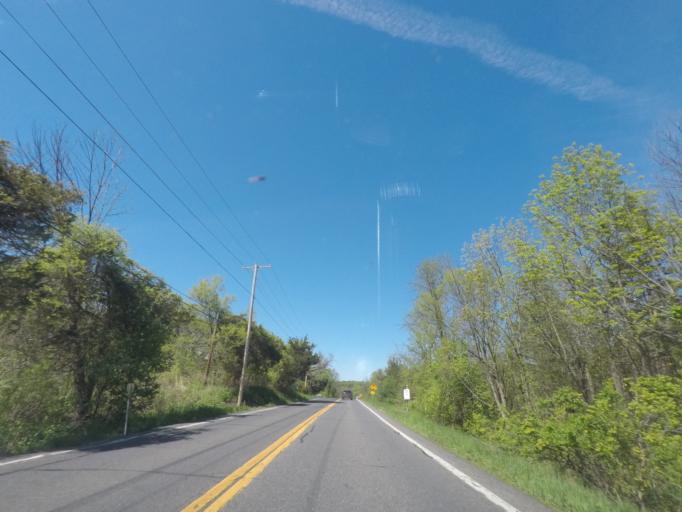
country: US
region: New York
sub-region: Ulster County
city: Saugerties
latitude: 42.1139
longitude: -73.9361
